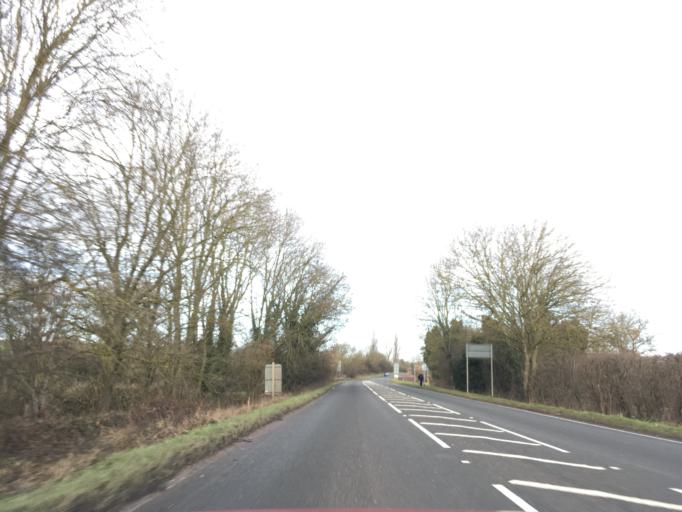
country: GB
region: England
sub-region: Nottinghamshire
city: East Leake
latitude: 52.8331
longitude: -1.1462
